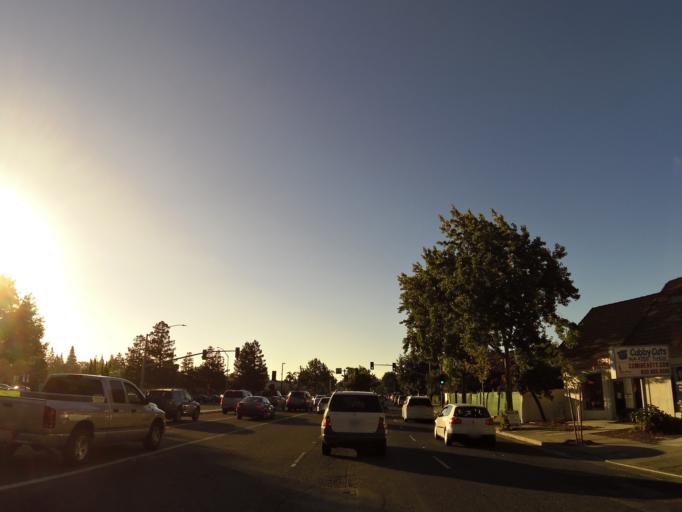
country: US
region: California
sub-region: Santa Clara County
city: Mountain View
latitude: 37.3914
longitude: -122.0946
